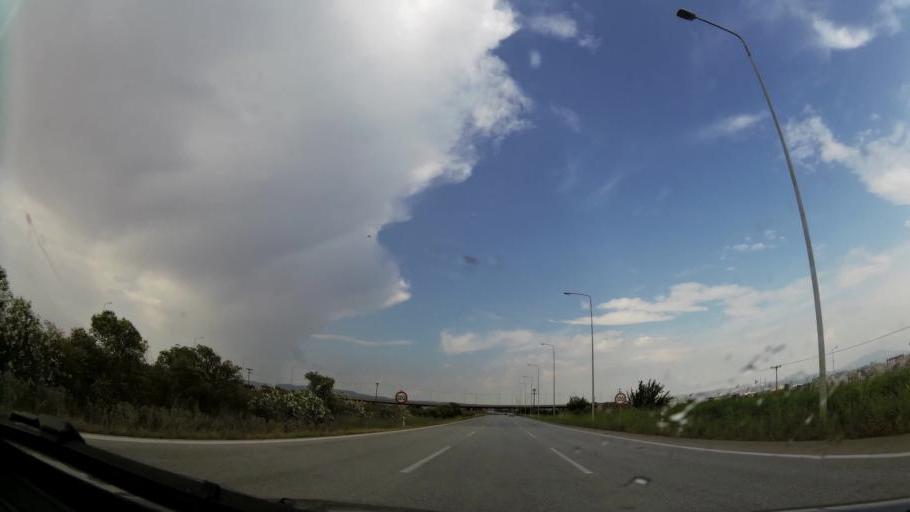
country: GR
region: Central Macedonia
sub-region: Nomos Thessalonikis
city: Sindos
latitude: 40.6476
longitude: 22.8094
